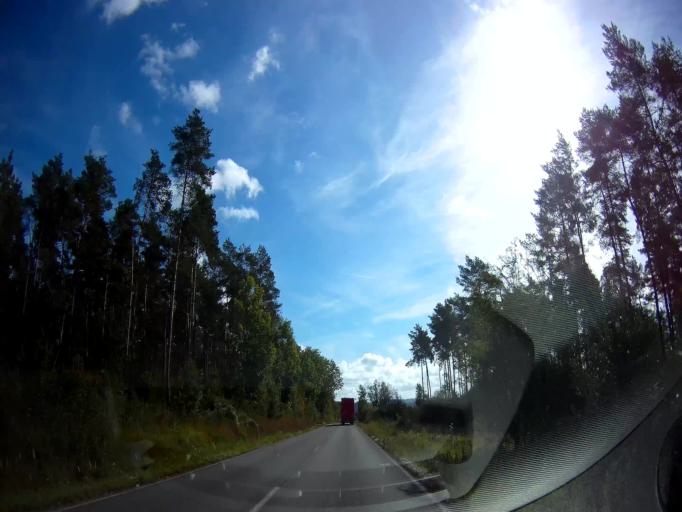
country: BE
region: Wallonia
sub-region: Province de Namur
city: Rochefort
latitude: 50.1674
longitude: 5.1801
